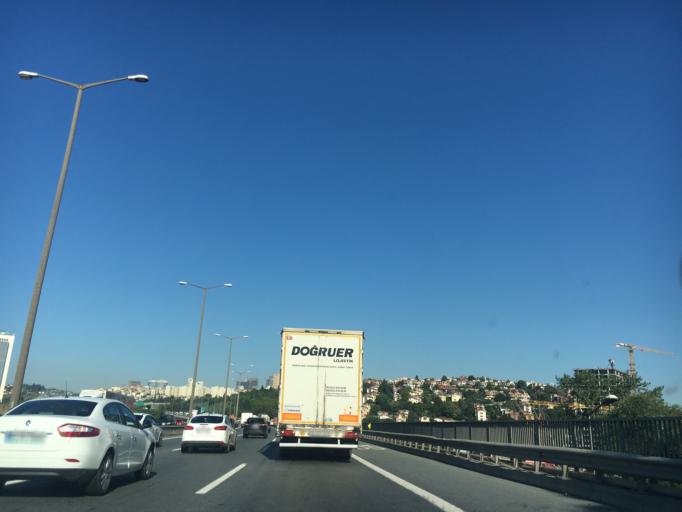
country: TR
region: Istanbul
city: Esenyurt
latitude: 41.0591
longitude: 28.7023
